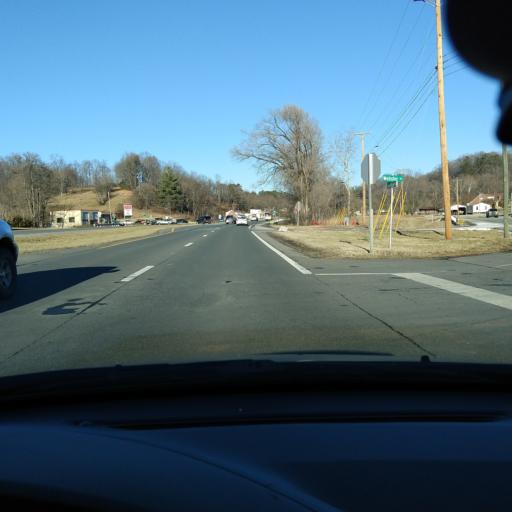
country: US
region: Virginia
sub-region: Botetourt County
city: Laymantown
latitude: 37.3347
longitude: -79.8597
